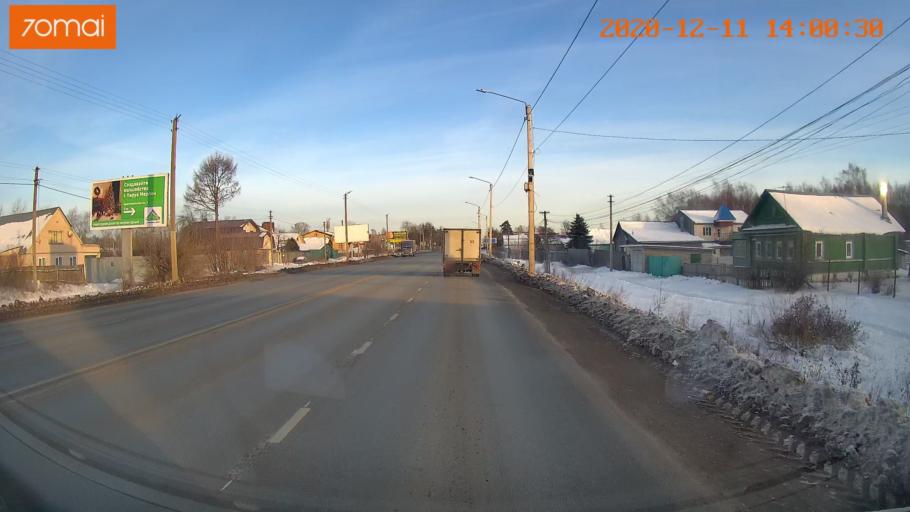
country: RU
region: Kostroma
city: Oktyabr'skiy
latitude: 57.7845
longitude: 41.0301
